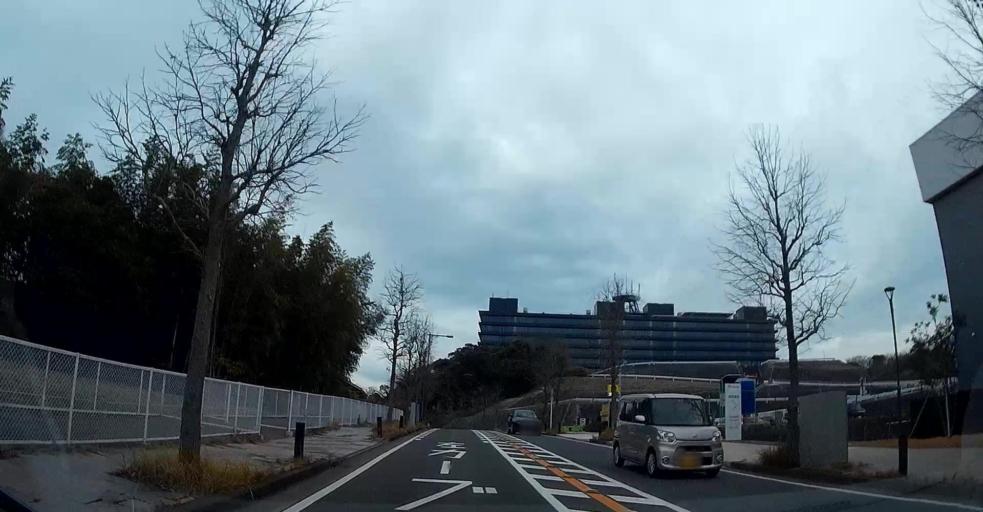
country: JP
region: Kanagawa
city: Yokosuka
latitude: 35.2247
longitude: 139.6666
